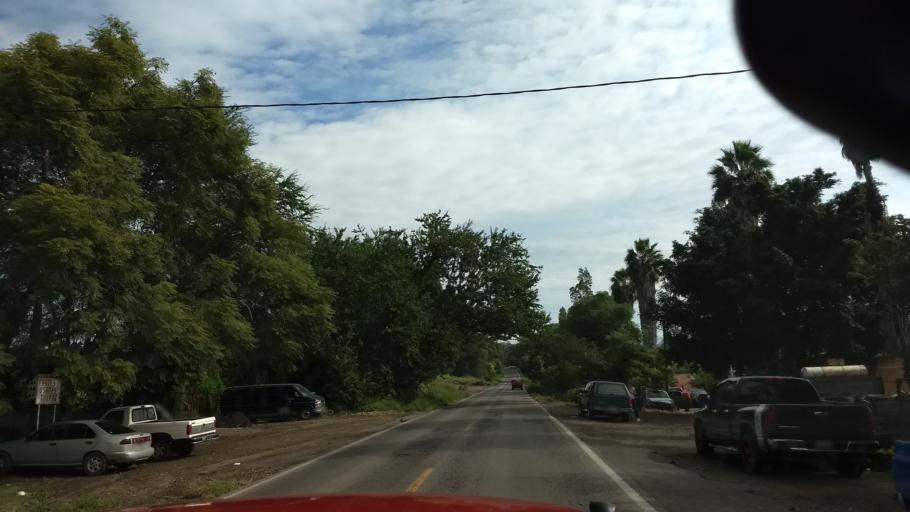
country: MX
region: Jalisco
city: Tuxpan
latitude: 19.5496
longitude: -103.3939
